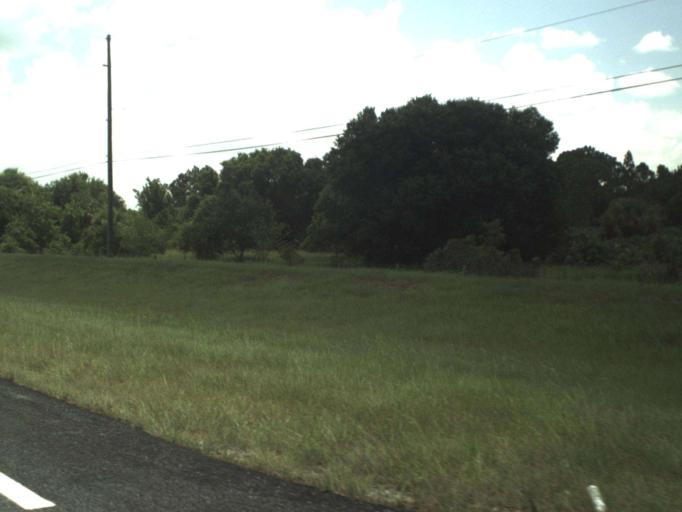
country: US
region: Florida
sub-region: Okeechobee County
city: Cypress Quarters
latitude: 27.3621
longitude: -80.6187
